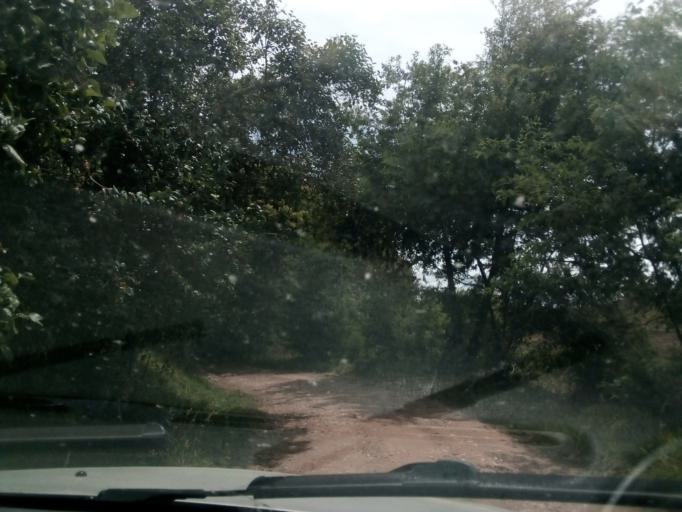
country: CO
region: Boyaca
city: Toca
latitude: 5.6133
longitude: -73.1132
